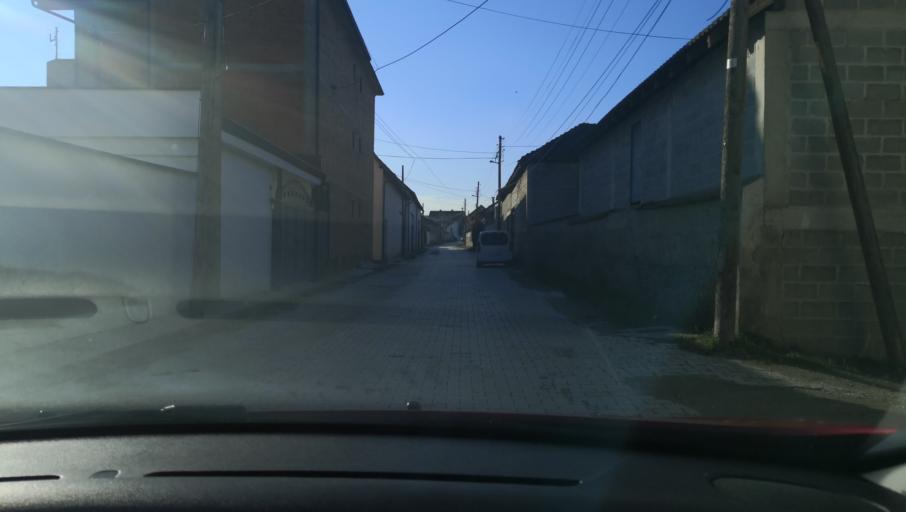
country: MK
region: Brvenica
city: Celopek
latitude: 41.9380
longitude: 21.0073
